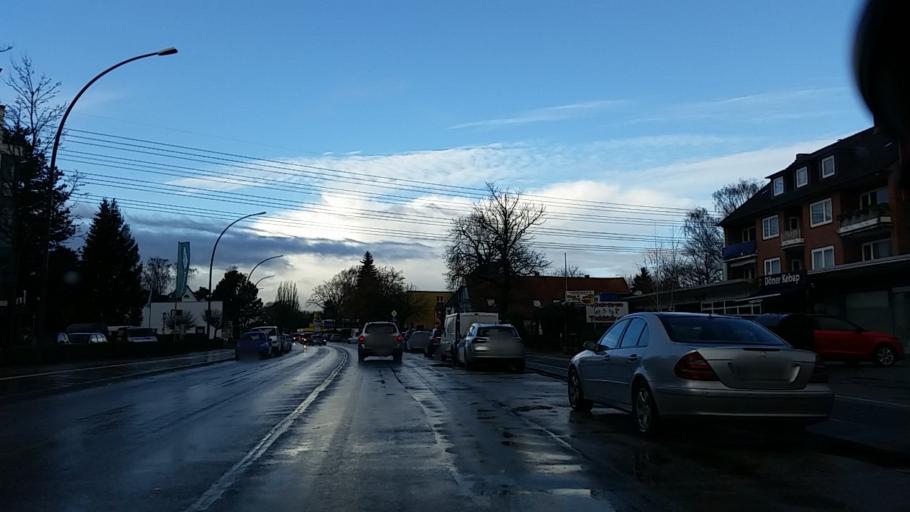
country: DE
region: Schleswig-Holstein
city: Halstenbek
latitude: 53.5977
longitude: 9.8623
